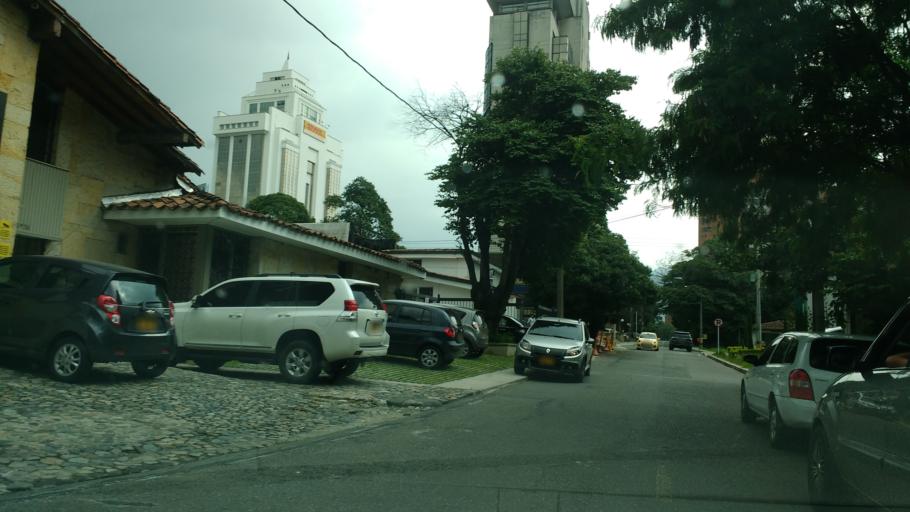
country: CO
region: Antioquia
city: Envigado
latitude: 6.1912
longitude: -75.5774
